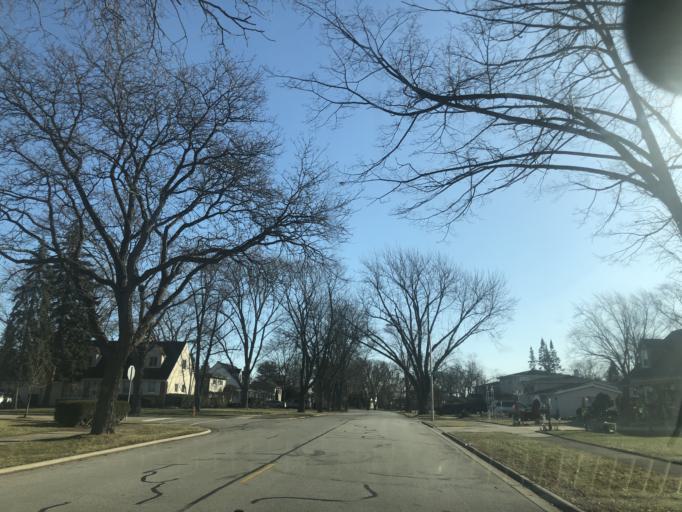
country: US
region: Illinois
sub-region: DuPage County
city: Addison
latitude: 41.9319
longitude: -88.0123
